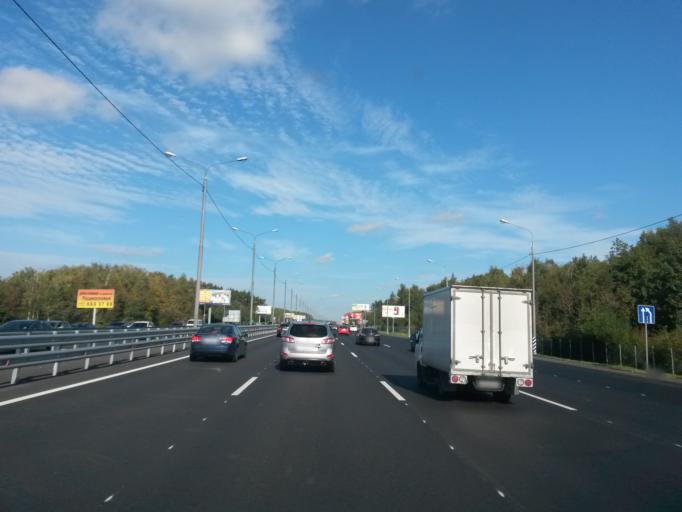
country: RU
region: Moskovskaya
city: Shcherbinka
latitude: 55.4872
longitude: 37.6129
